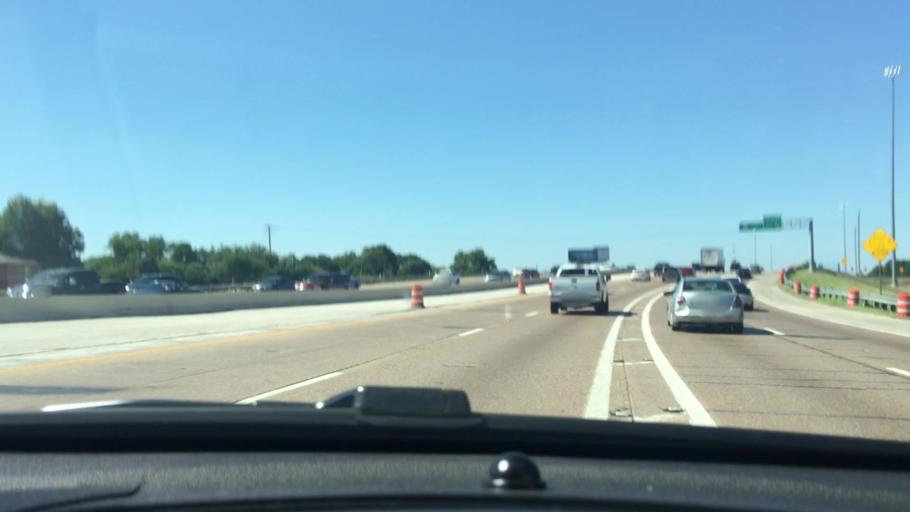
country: US
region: Texas
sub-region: Dallas County
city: Cockrell Hill
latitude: 32.7113
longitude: -96.8299
